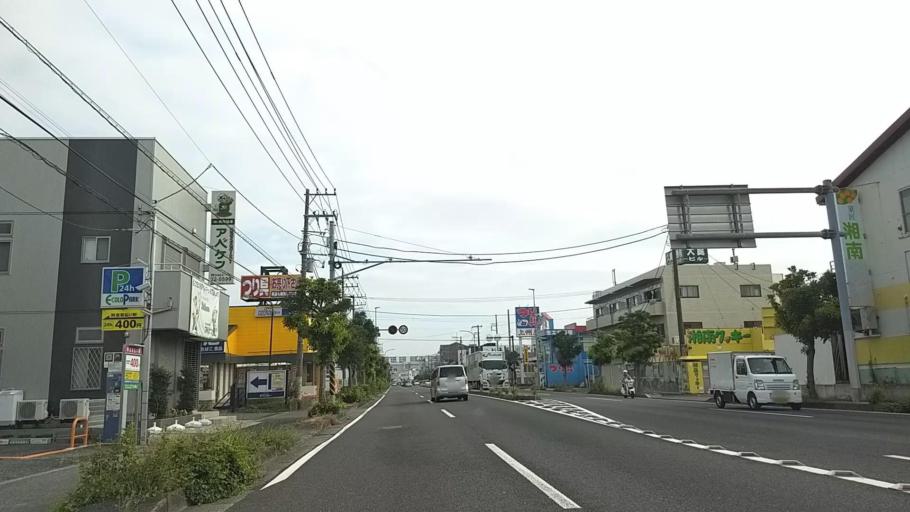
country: JP
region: Kanagawa
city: Hiratsuka
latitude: 35.3454
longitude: 139.3564
